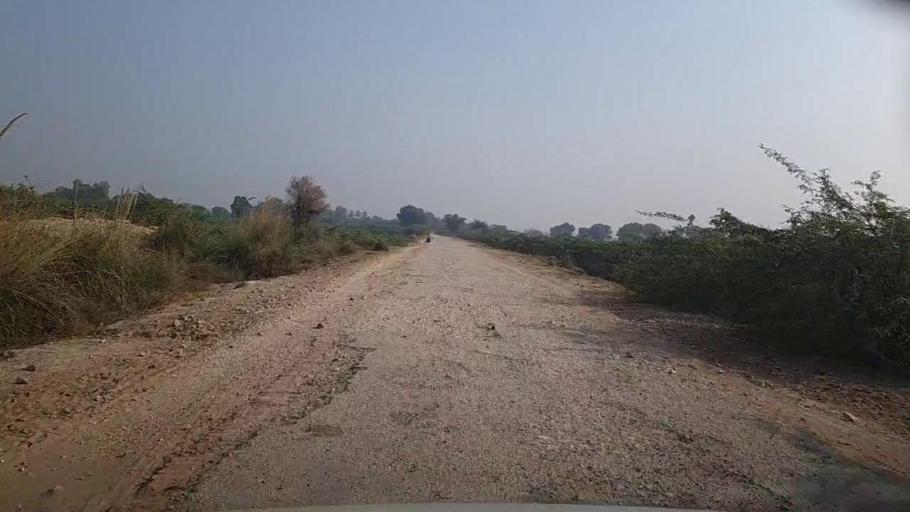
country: PK
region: Sindh
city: Setharja Old
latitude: 27.0615
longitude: 68.4576
